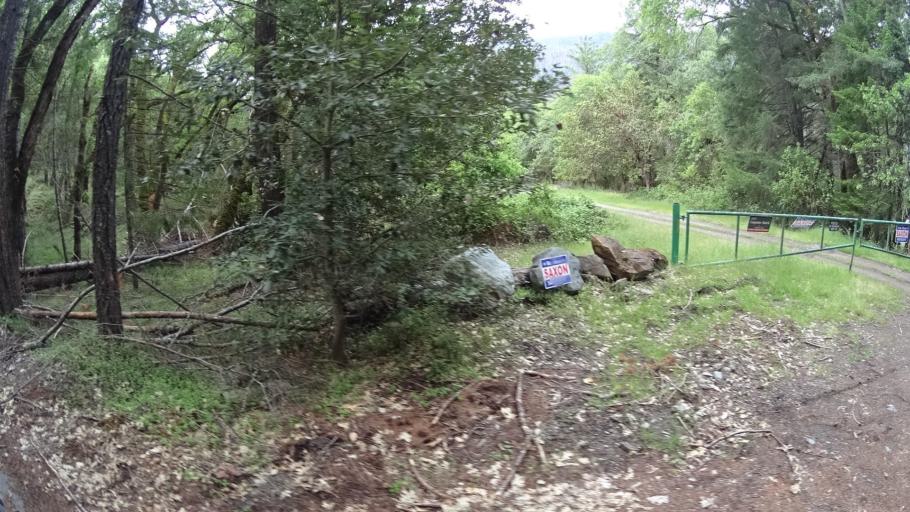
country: US
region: California
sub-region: Humboldt County
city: Willow Creek
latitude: 40.9290
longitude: -123.6155
